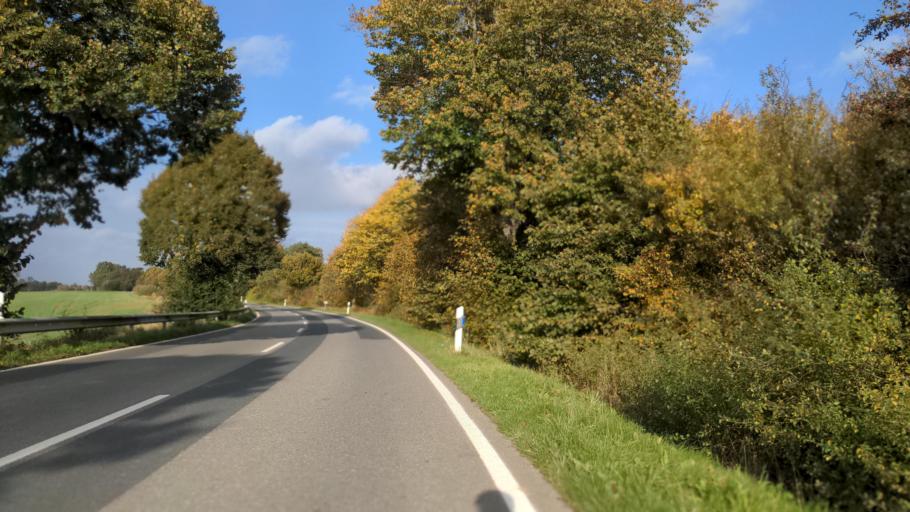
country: DE
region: Schleswig-Holstein
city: Beschendorf
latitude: 54.1683
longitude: 10.8730
